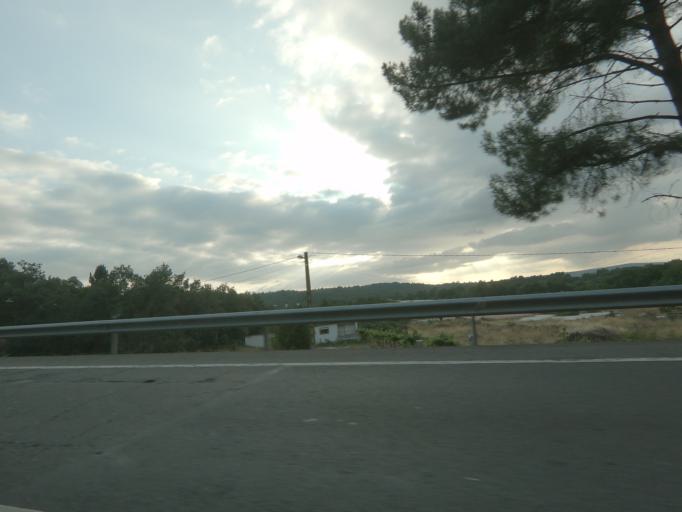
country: ES
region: Galicia
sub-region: Provincia de Ourense
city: Taboadela
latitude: 42.2739
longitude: -7.8376
